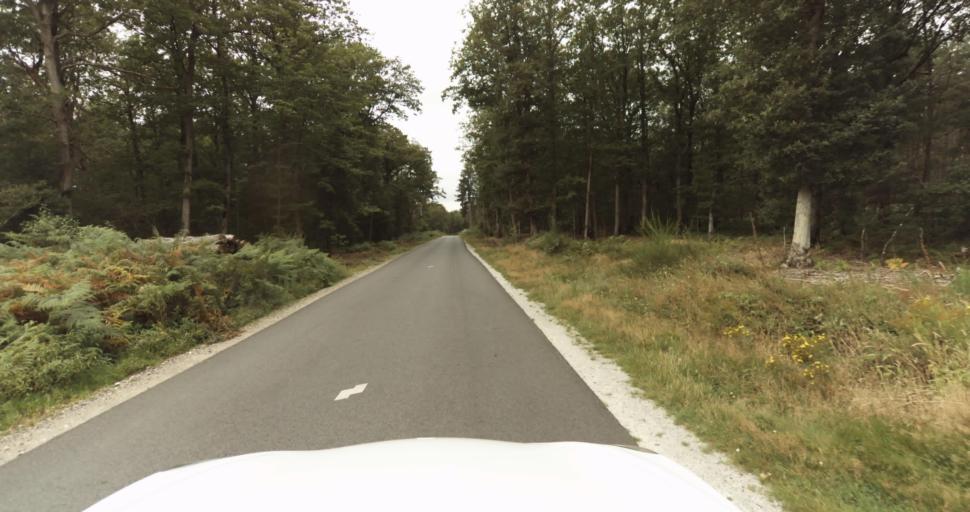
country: FR
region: Haute-Normandie
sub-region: Departement de l'Eure
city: Saint-Sebastien-de-Morsent
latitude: 48.9642
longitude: 1.0515
